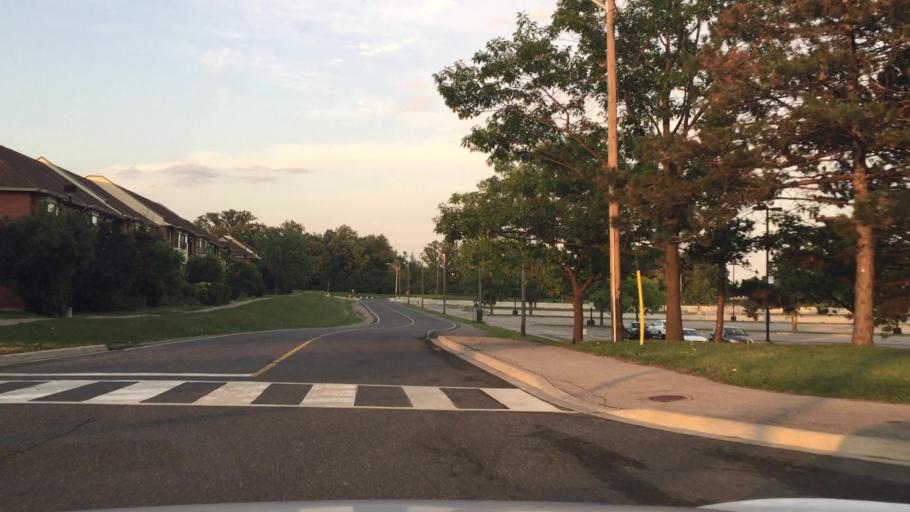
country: CA
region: Ontario
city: Concord
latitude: 43.7754
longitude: -79.5002
